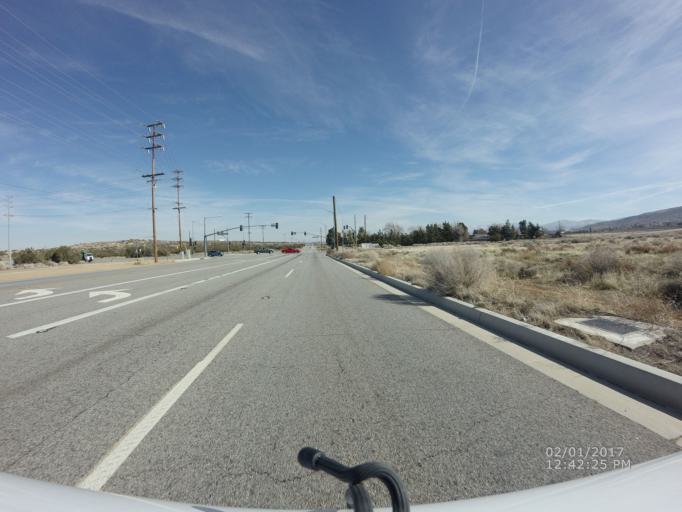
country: US
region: California
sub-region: Los Angeles County
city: Palmdale
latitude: 34.5579
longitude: -118.1421
